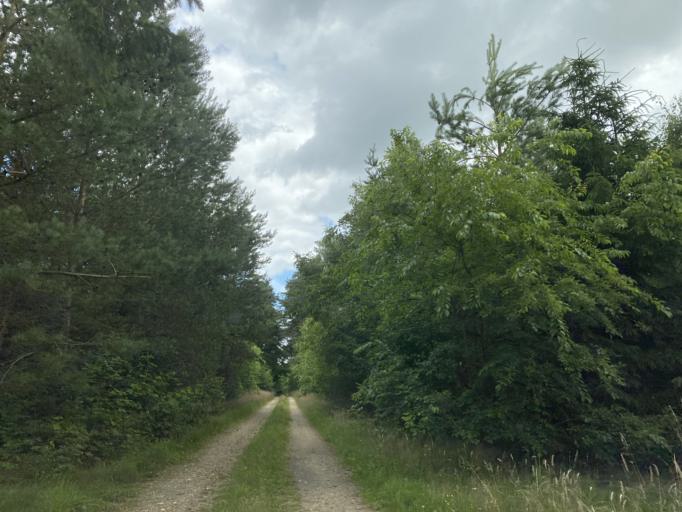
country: DK
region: Central Jutland
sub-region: Viborg Kommune
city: Bjerringbro
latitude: 56.2762
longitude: 9.6555
